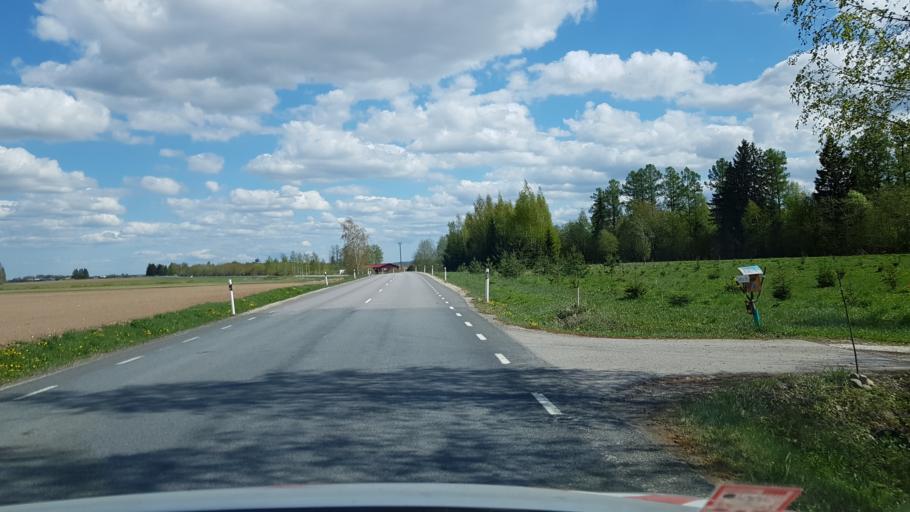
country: EE
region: Tartu
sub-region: UElenurme vald
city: Ulenurme
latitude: 58.3107
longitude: 26.6701
